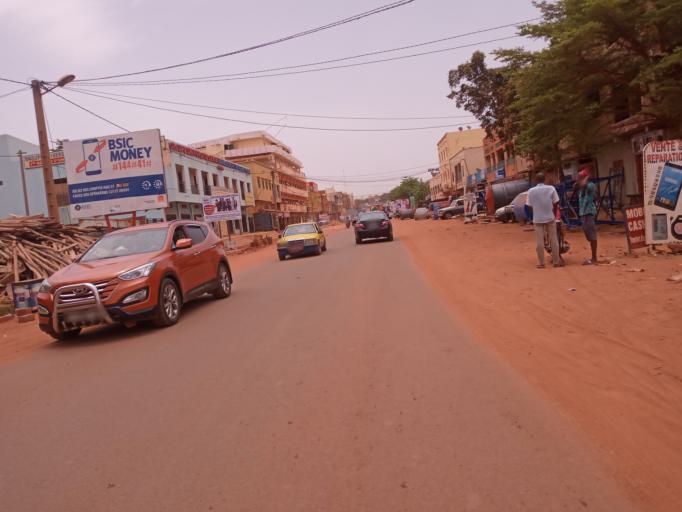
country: ML
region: Bamako
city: Bamako
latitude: 12.5766
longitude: -8.0117
